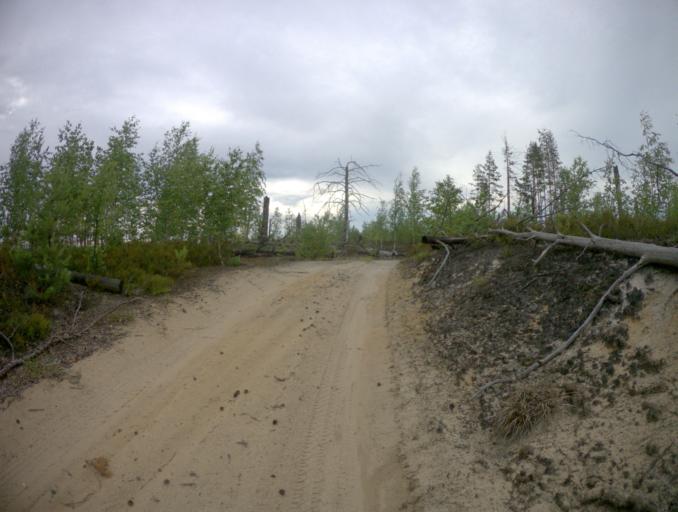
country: RU
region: Nizjnij Novgorod
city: Frolishchi
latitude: 56.5406
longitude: 42.6581
